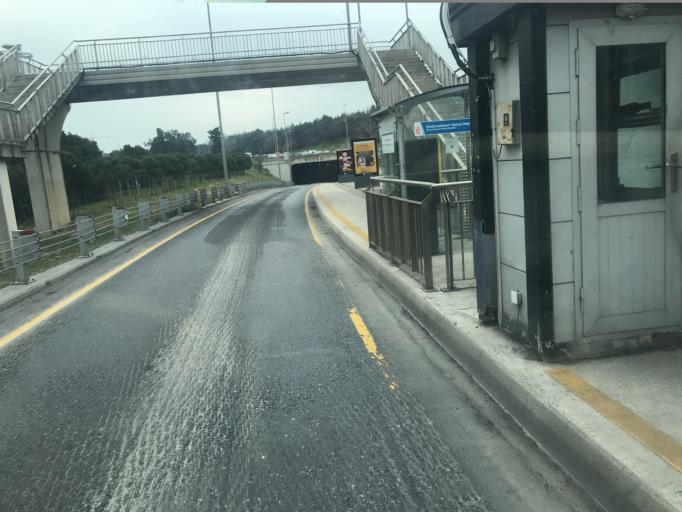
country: TR
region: Istanbul
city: UEskuedar
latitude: 41.0320
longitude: 29.0470
